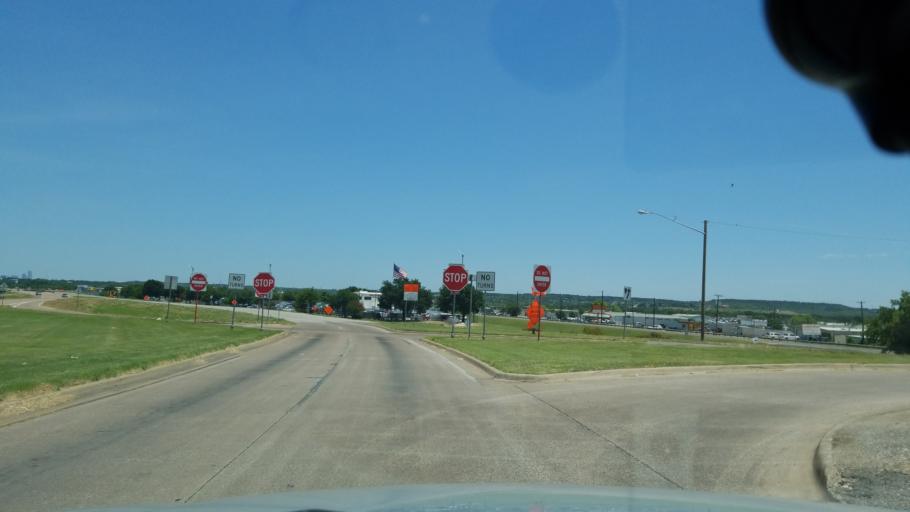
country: US
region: Texas
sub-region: Dallas County
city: Grand Prairie
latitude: 32.7474
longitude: -96.9511
